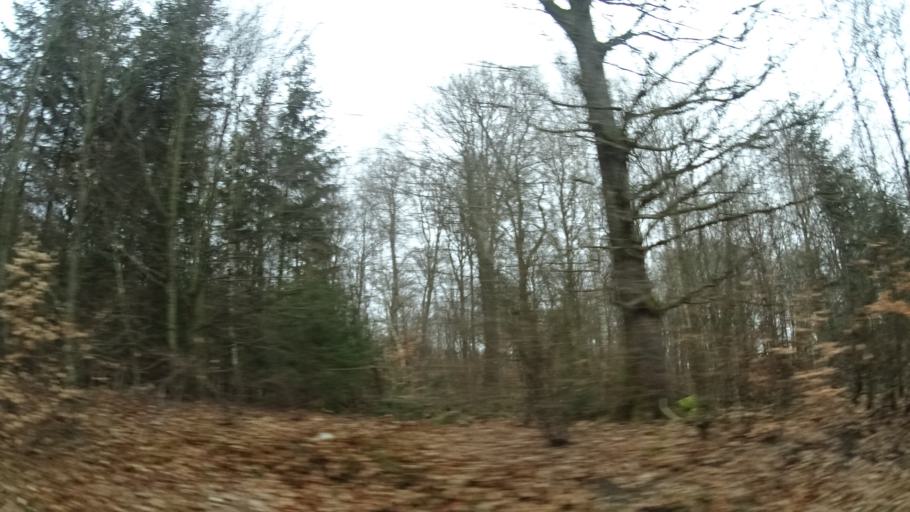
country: DE
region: Rheinland-Pfalz
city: Ippenschied
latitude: 49.8953
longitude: 7.6184
